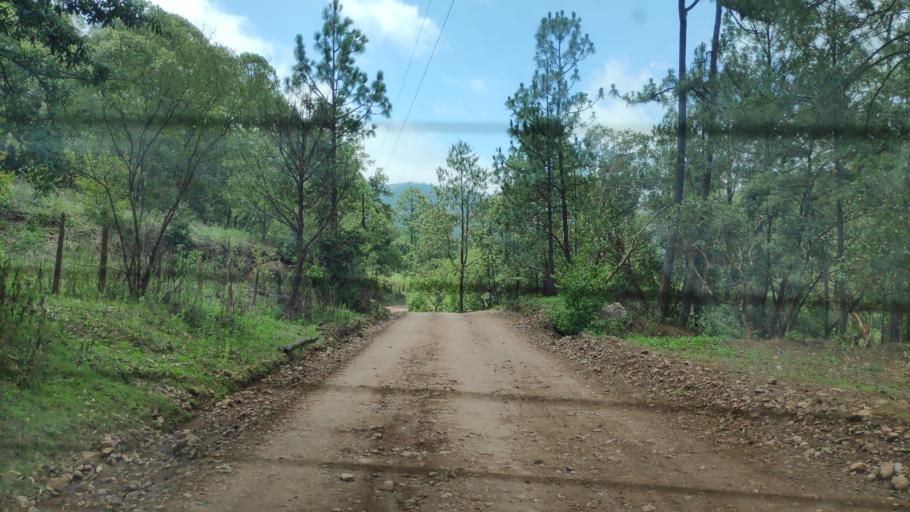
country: MX
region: Sinaloa
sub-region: Sinaloa
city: Bacubirito
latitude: 25.8566
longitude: -107.5873
